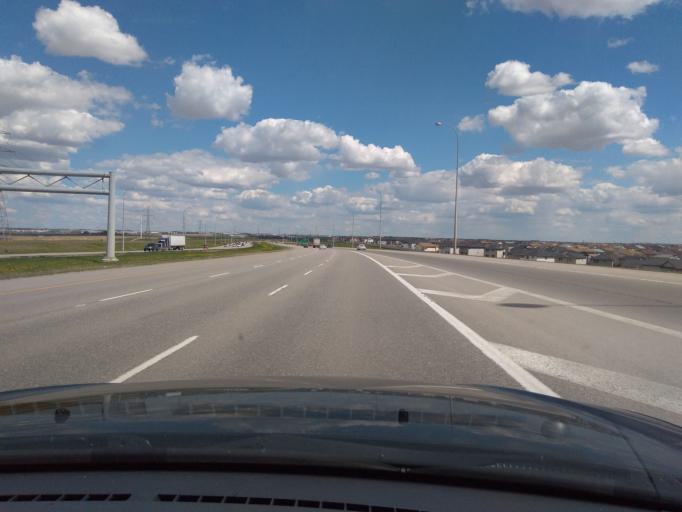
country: CA
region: Alberta
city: Calgary
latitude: 51.1730
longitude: -114.0600
